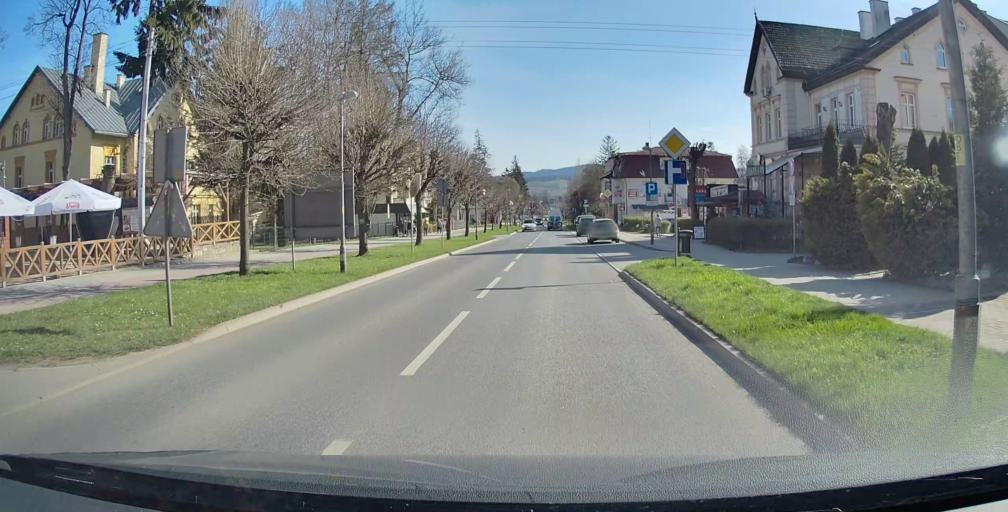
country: PL
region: Lower Silesian Voivodeship
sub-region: Powiat klodzki
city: Kudowa-Zdroj
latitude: 50.4418
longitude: 16.2413
